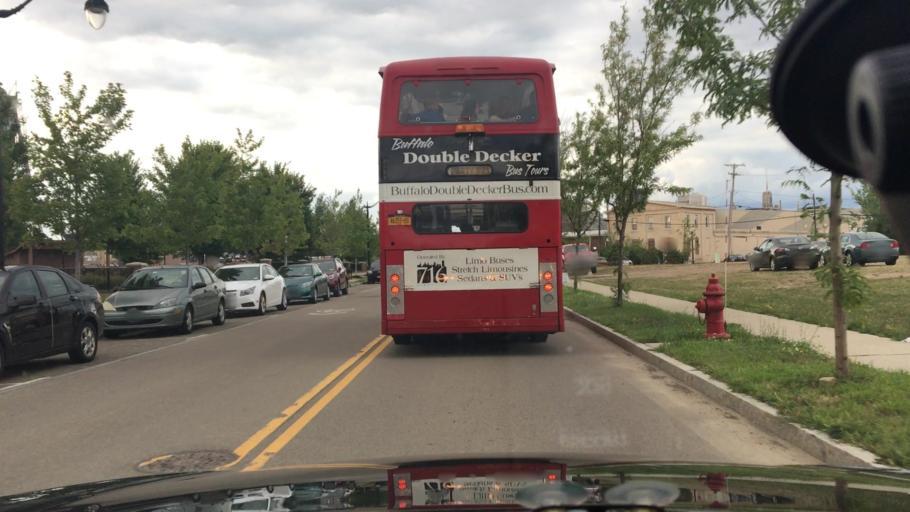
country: US
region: New York
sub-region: Erie County
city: Buffalo
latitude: 42.8705
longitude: -78.8699
